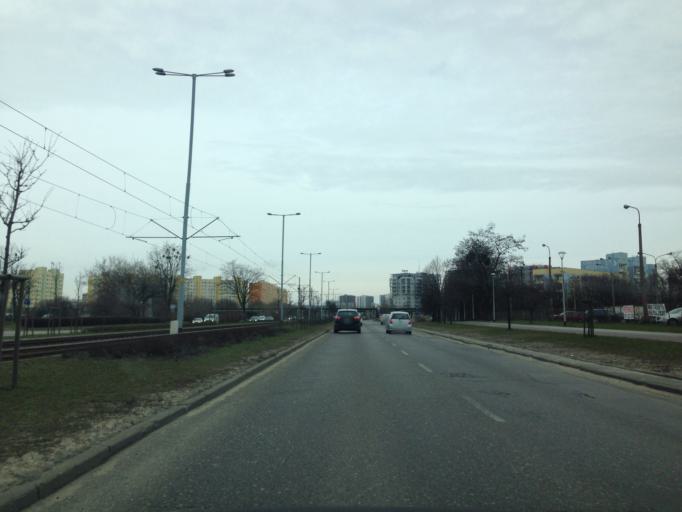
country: PL
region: Pomeranian Voivodeship
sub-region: Gdansk
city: Gdansk
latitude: 54.3925
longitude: 18.6052
